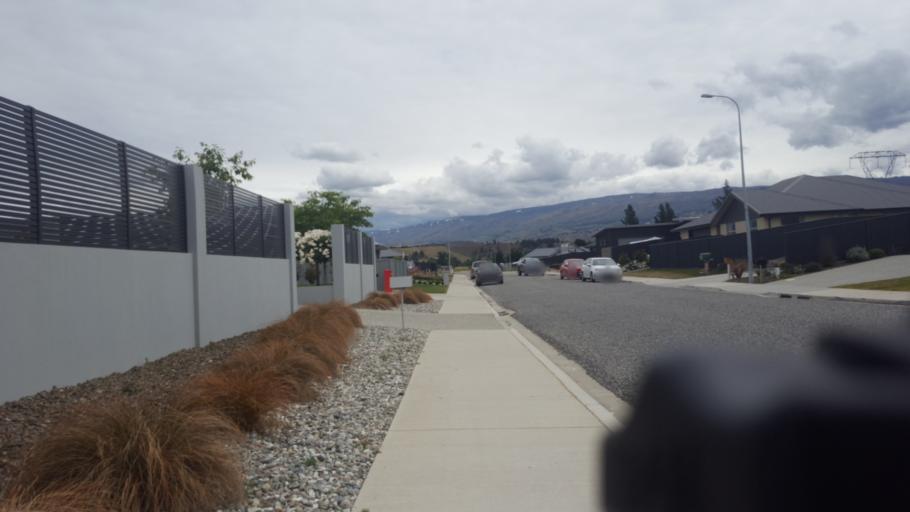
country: NZ
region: Otago
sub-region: Queenstown-Lakes District
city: Wanaka
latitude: -45.2439
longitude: 169.3740
